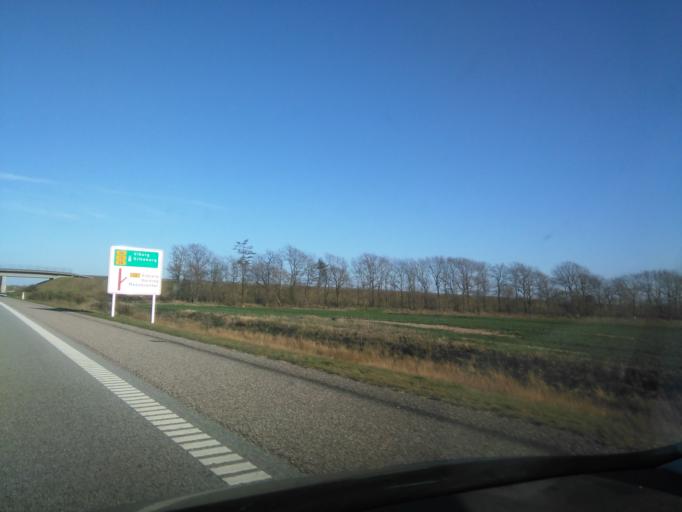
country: DK
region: Central Jutland
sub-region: Herning Kommune
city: Snejbjerg
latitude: 56.1134
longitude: 8.9316
